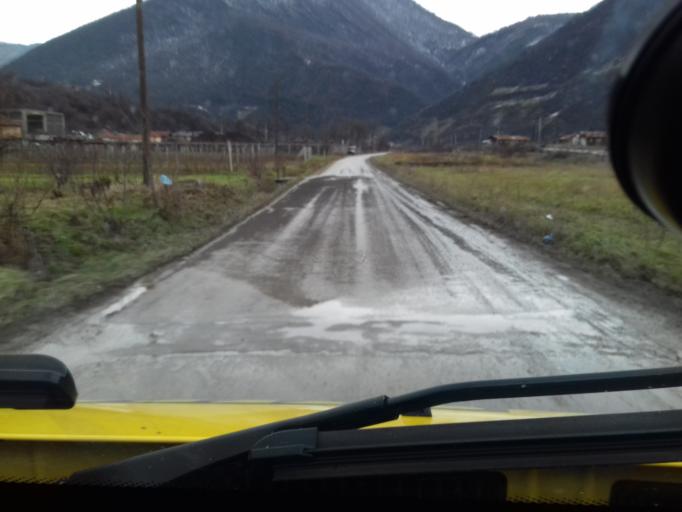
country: BA
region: Federation of Bosnia and Herzegovina
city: Zenica
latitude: 44.2458
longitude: 17.8968
